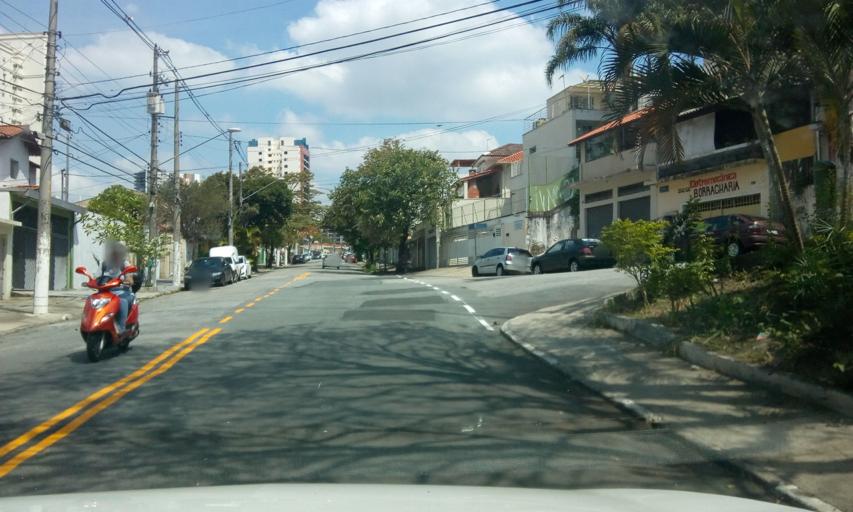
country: BR
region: Sao Paulo
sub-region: Sao Paulo
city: Sao Paulo
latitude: -23.5319
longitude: -46.7063
